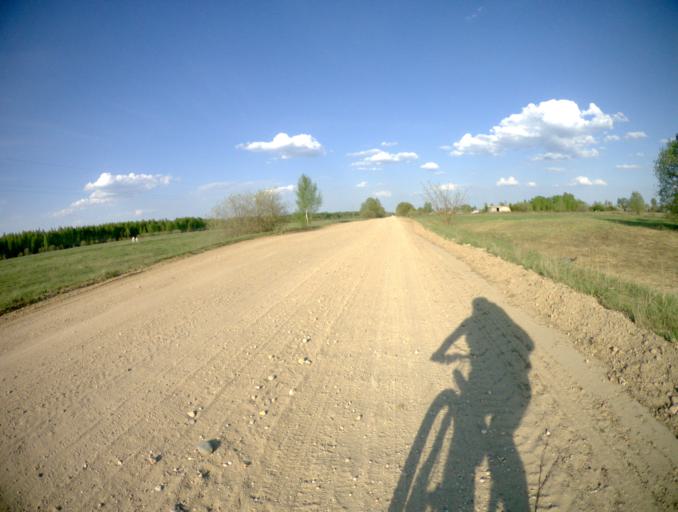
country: RU
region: Vladimir
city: Mstera
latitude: 56.5509
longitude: 41.6905
